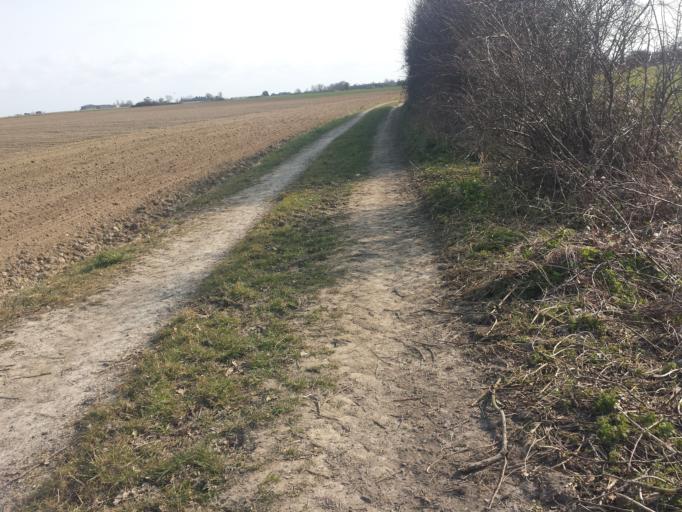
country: GB
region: England
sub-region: Essex
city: Little Clacton
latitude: 51.8941
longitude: 1.1626
